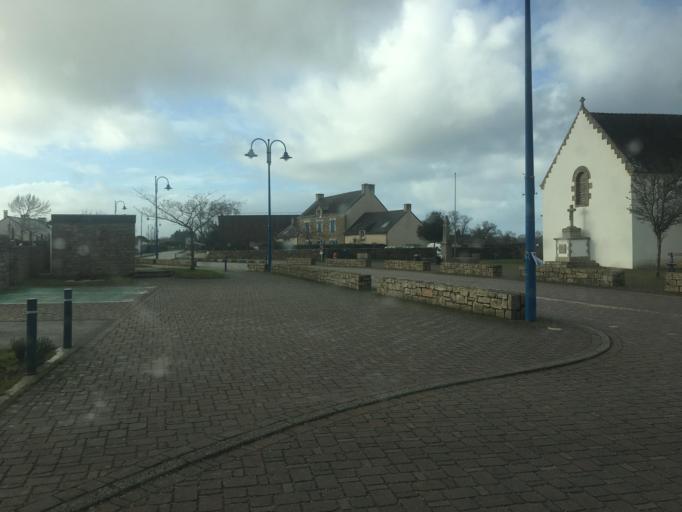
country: FR
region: Brittany
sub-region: Departement du Morbihan
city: Surzur
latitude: 47.5259
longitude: -2.6478
